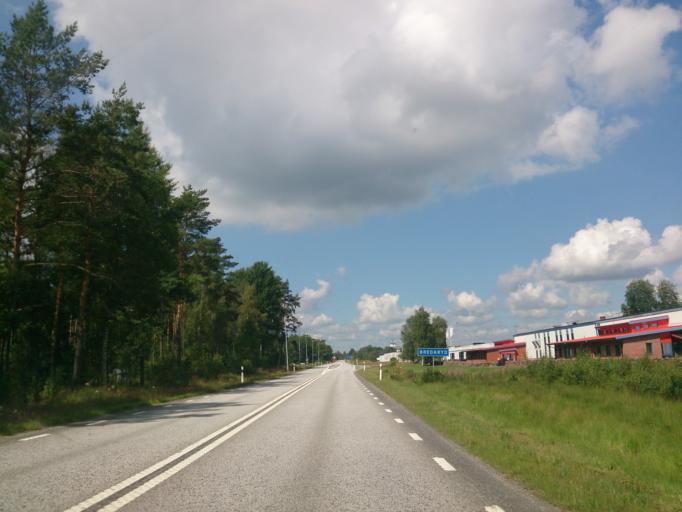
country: SE
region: Joenkoeping
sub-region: Varnamo Kommun
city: Bredaryd
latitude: 57.1702
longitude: 13.7559
